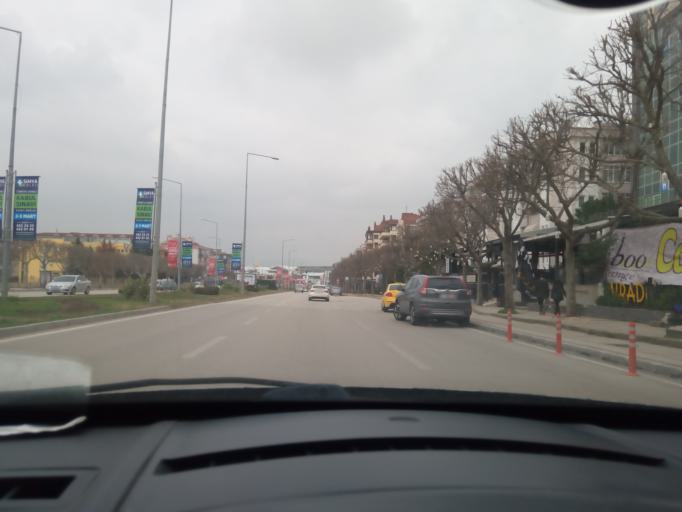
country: TR
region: Bursa
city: Yildirim
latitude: 40.2250
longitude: 28.9793
